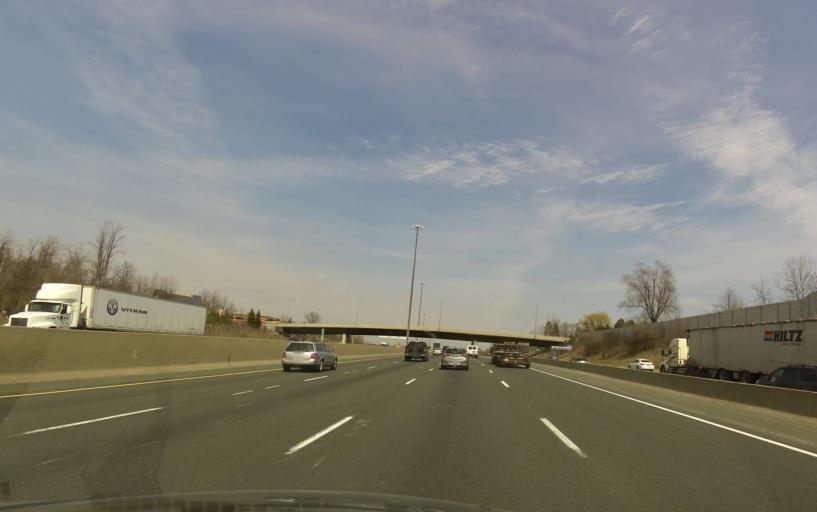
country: CA
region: Ontario
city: Pickering
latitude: 43.8065
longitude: -79.1306
